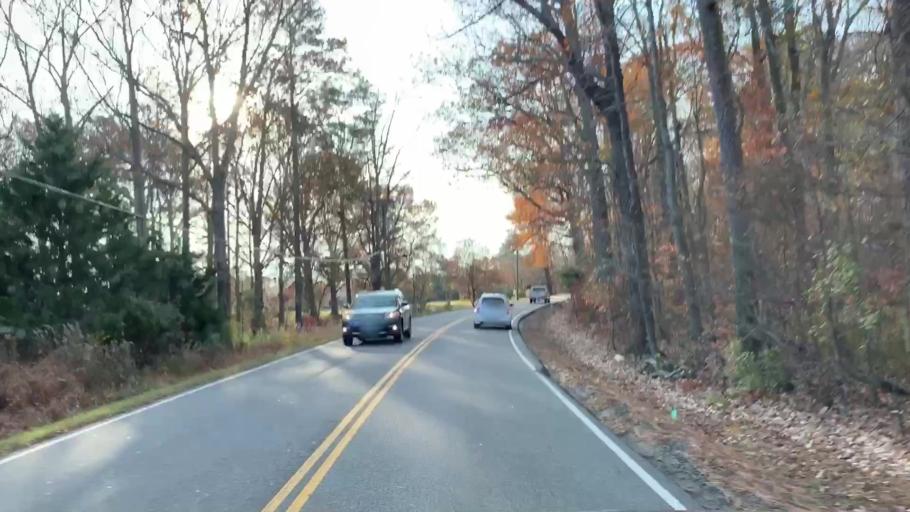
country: US
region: Virginia
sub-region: City of Chesapeake
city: Chesapeake
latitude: 36.7664
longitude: -76.1500
